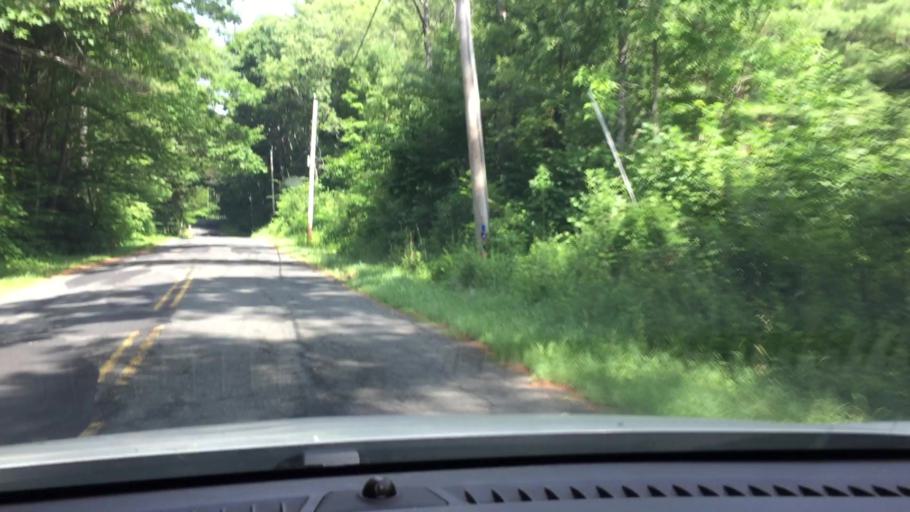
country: US
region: Massachusetts
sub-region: Berkshire County
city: Otis
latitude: 42.1879
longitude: -73.1513
